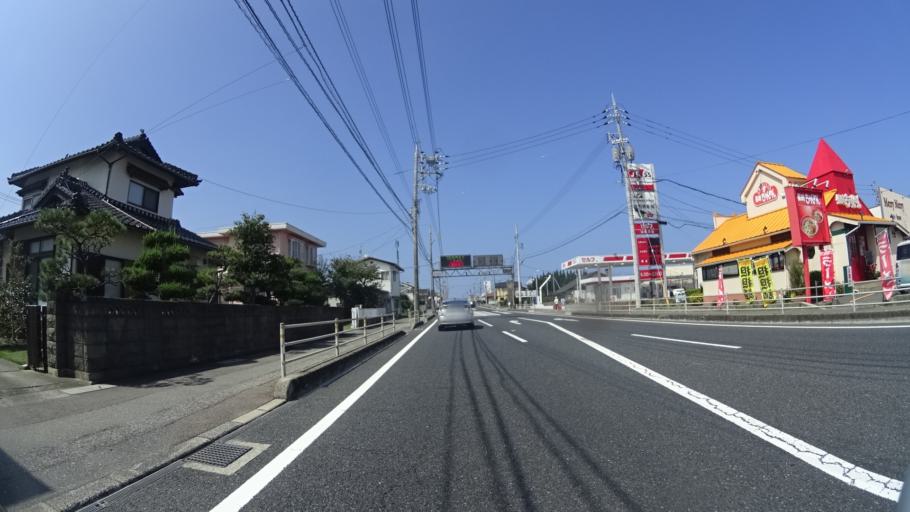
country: JP
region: Shimane
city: Masuda
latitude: 34.6897
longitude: 131.8157
